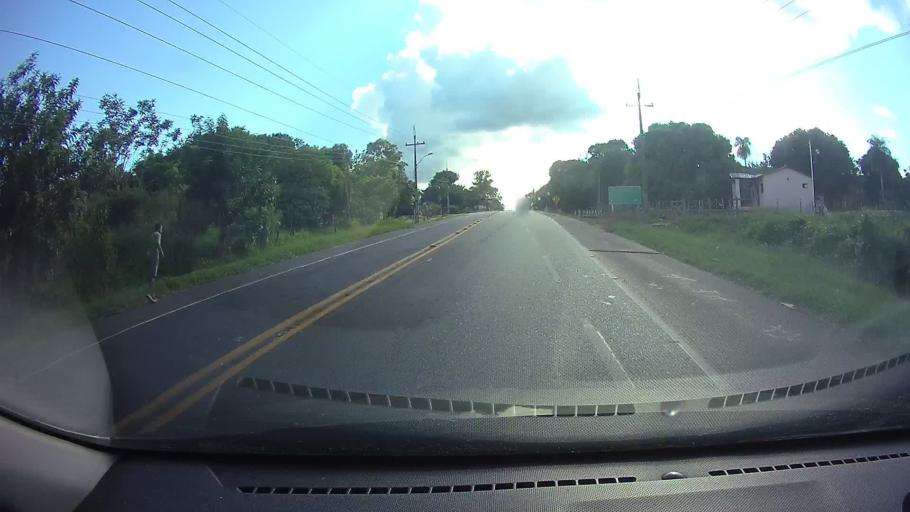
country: PY
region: Cordillera
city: Eusebio Ayala
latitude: -25.3815
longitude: -57.0430
